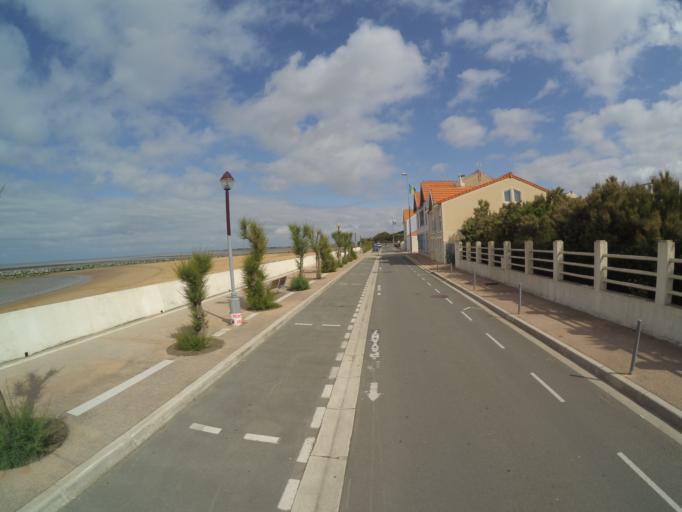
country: FR
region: Poitou-Charentes
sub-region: Departement de la Charente-Maritime
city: Chatelaillon-Plage
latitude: 46.0816
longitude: -1.0959
